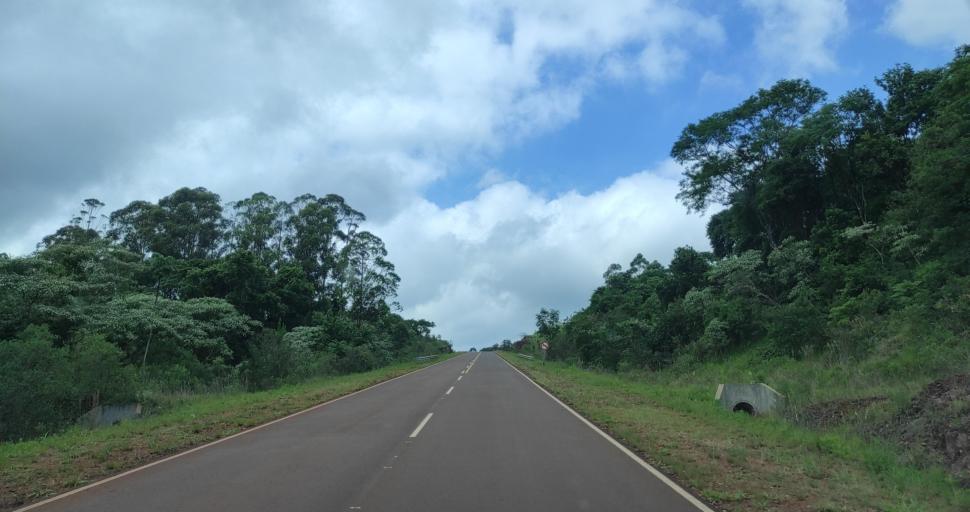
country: AR
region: Misiones
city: Campo Grande
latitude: -27.3160
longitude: -54.8986
